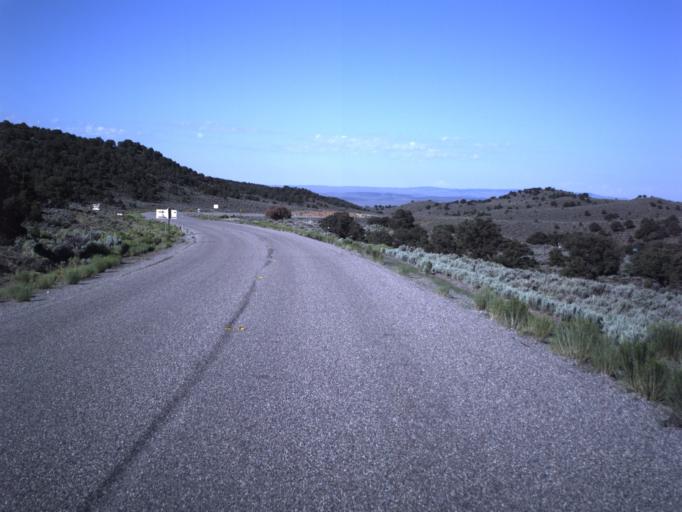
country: US
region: Utah
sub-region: Wayne County
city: Loa
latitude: 38.4910
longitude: -111.5402
